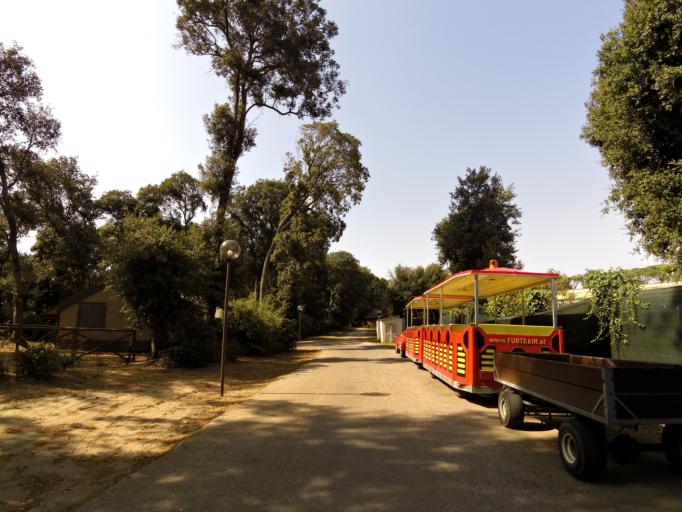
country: IT
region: Tuscany
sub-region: Provincia di Livorno
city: Donoratico
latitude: 43.1532
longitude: 10.5462
